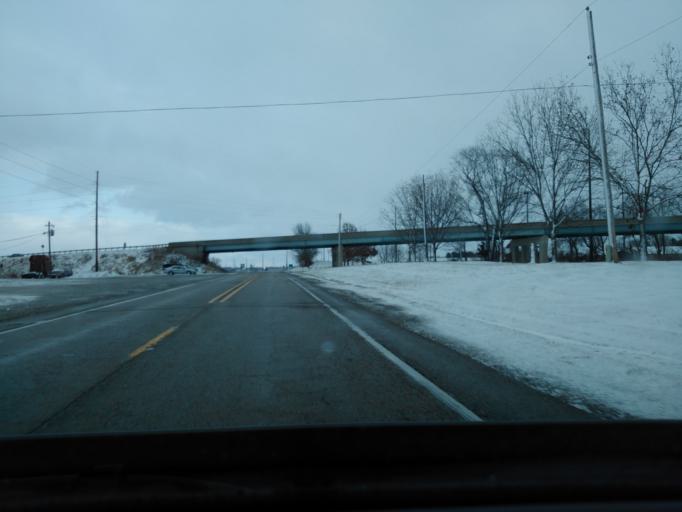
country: US
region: Illinois
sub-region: Madison County
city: Saint Jacob
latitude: 38.7161
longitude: -89.8038
